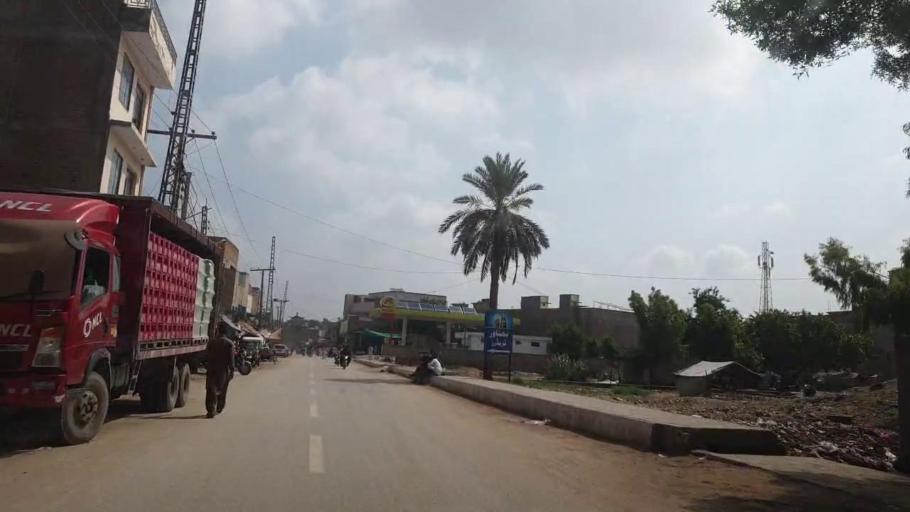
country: PK
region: Sindh
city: Khairpur
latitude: 27.5320
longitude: 68.7492
